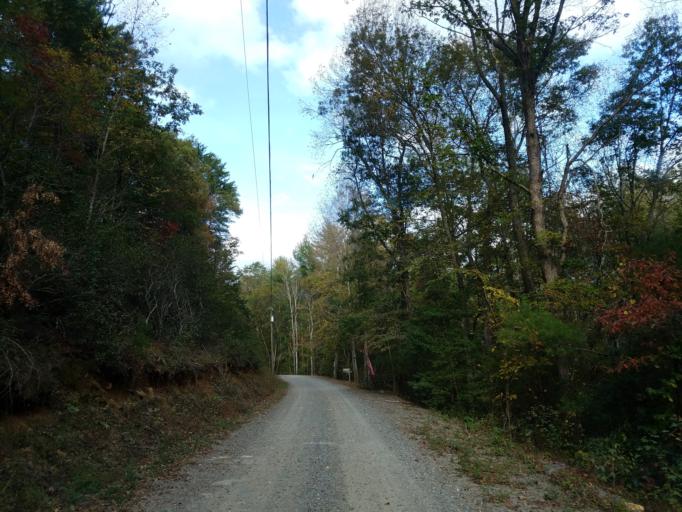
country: US
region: Georgia
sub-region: Dawson County
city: Dawsonville
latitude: 34.6281
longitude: -84.2441
